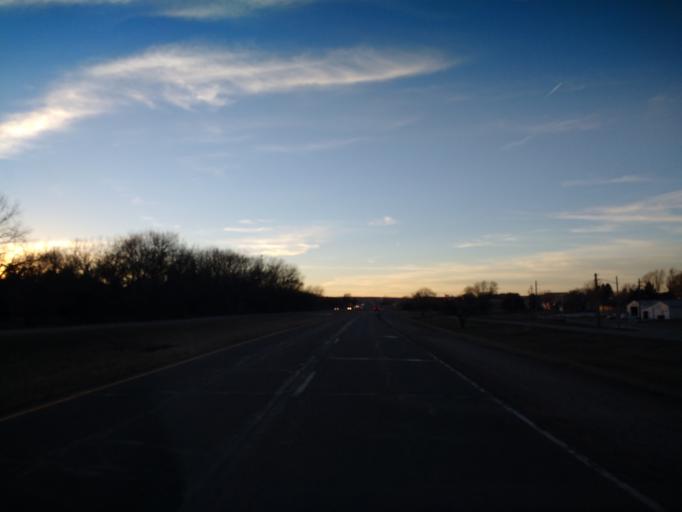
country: US
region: Iowa
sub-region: Woodbury County
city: Moville
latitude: 42.4819
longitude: -96.0700
